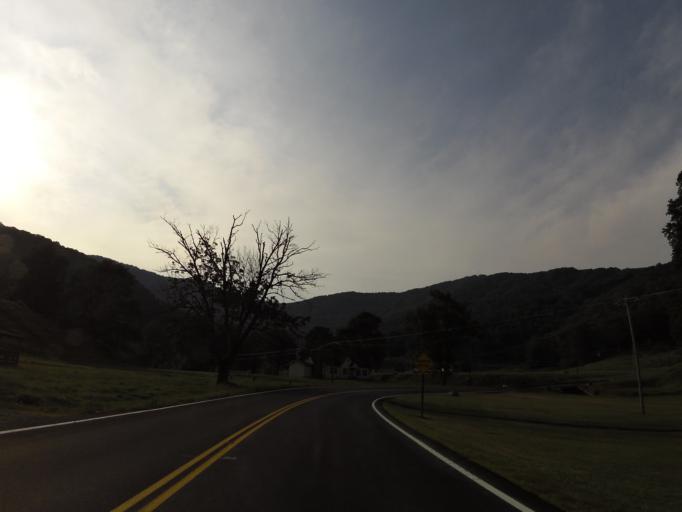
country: US
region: Tennessee
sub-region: Morgan County
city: Coalfield
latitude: 36.1008
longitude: -84.4467
